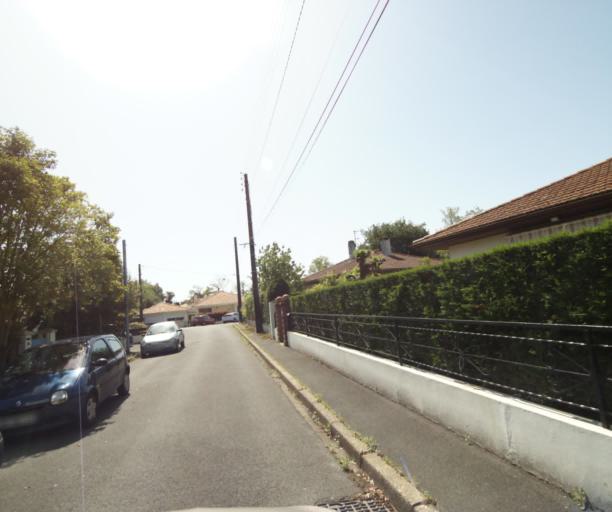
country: FR
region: Aquitaine
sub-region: Departement des Pyrenees-Atlantiques
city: Bayonne
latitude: 43.4763
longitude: -1.4636
